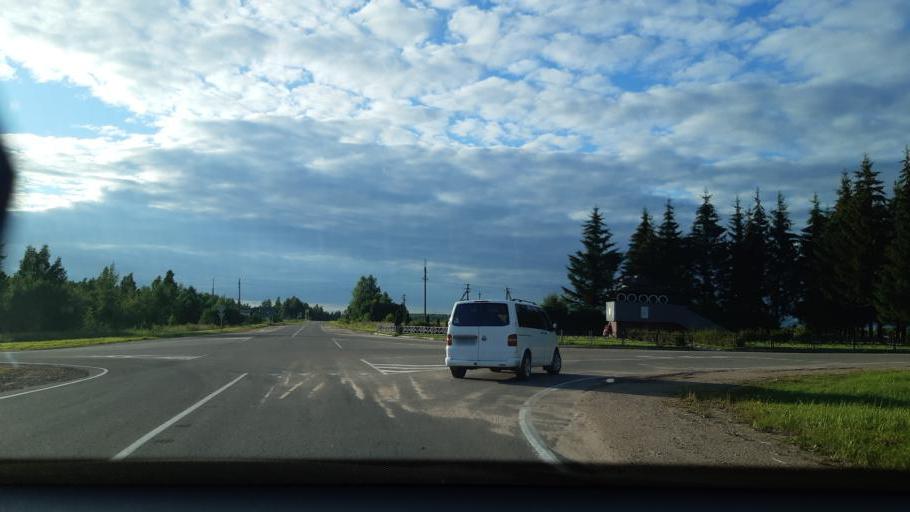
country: RU
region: Smolensk
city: Yel'nya
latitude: 54.5674
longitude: 33.1524
